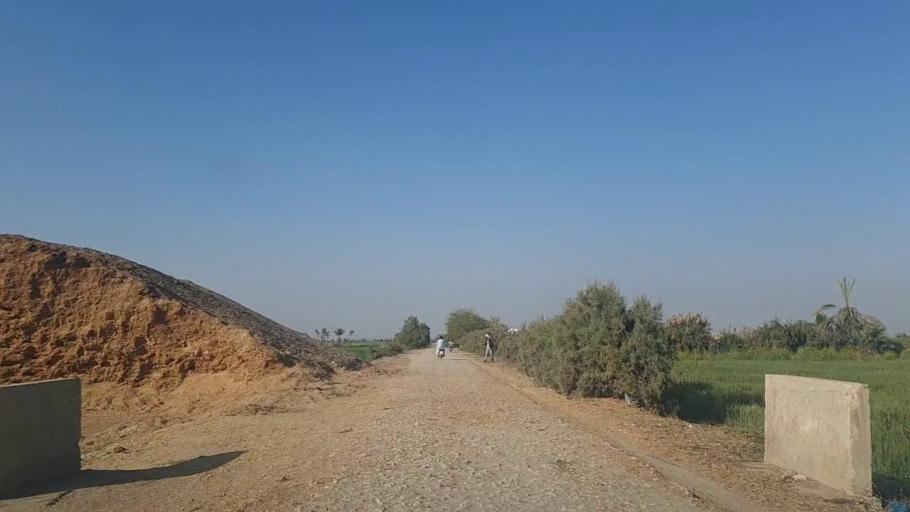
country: PK
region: Sindh
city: Jam Sahib
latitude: 26.3219
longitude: 68.7146
